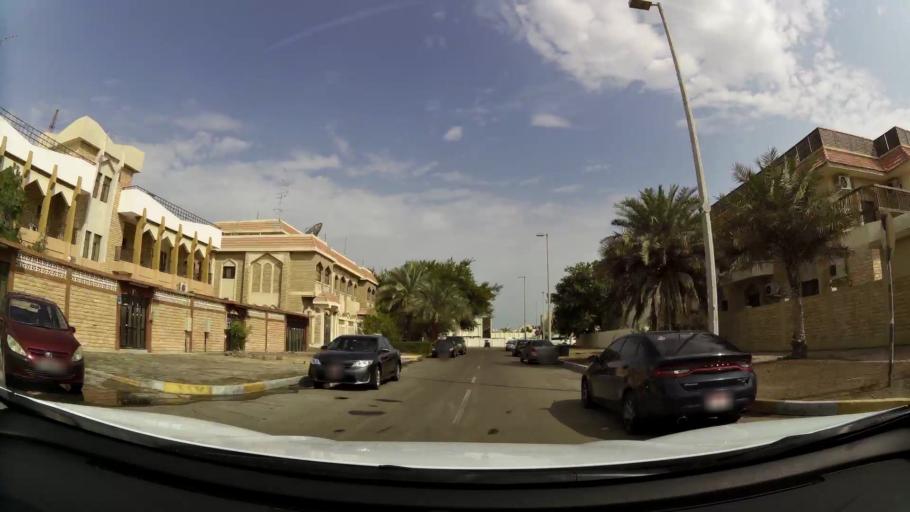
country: AE
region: Abu Dhabi
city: Abu Dhabi
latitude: 24.4372
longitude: 54.4288
